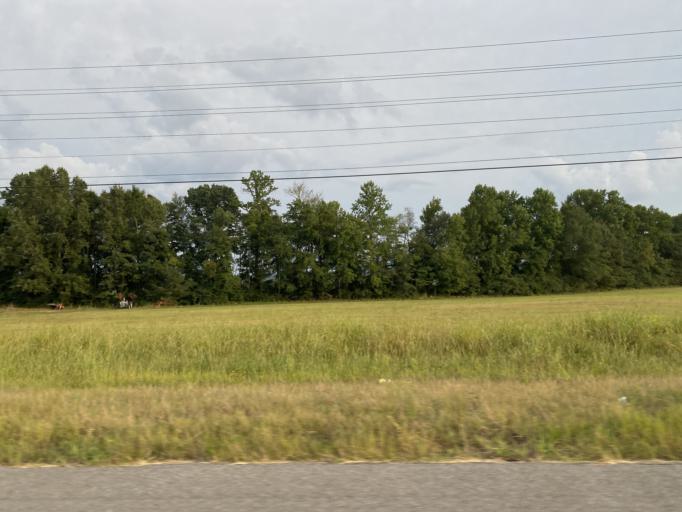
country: US
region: Alabama
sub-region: Franklin County
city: Red Bay
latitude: 34.4491
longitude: -88.0781
